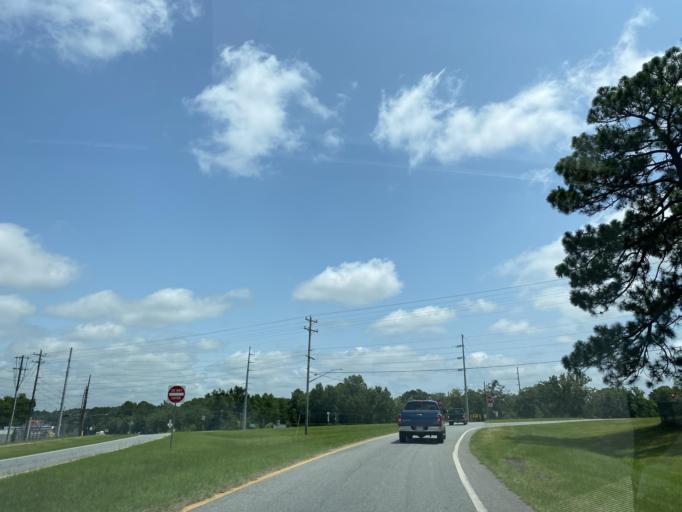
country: US
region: Georgia
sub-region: Telfair County
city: McRae
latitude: 32.0486
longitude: -82.9113
